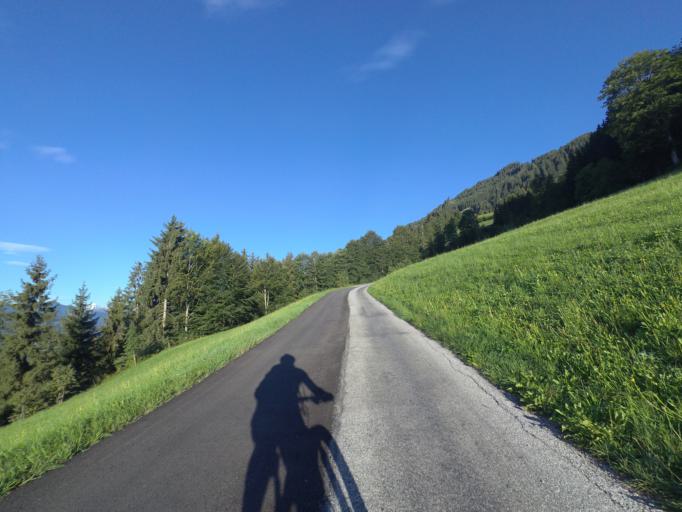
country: AT
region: Salzburg
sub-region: Politischer Bezirk Sankt Johann im Pongau
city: Goldegg
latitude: 47.3389
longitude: 13.1032
